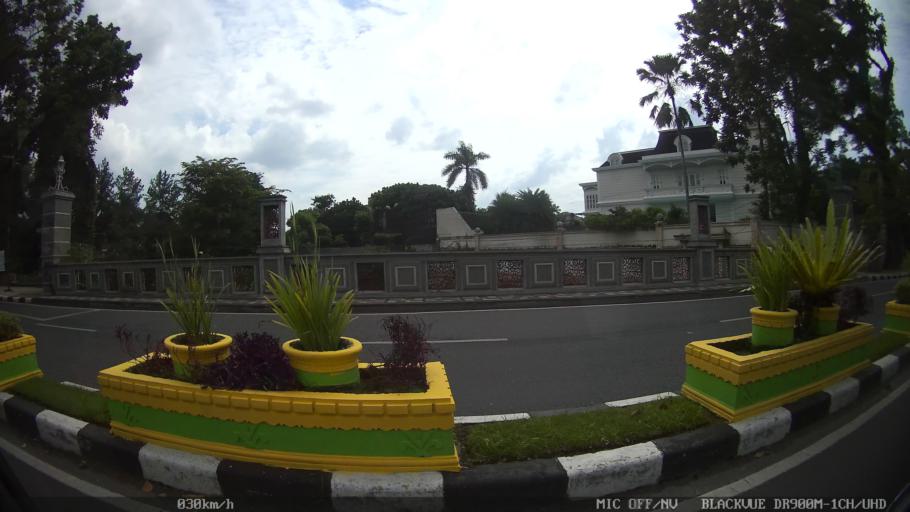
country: ID
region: North Sumatra
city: Medan
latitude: 3.5769
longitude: 98.6677
